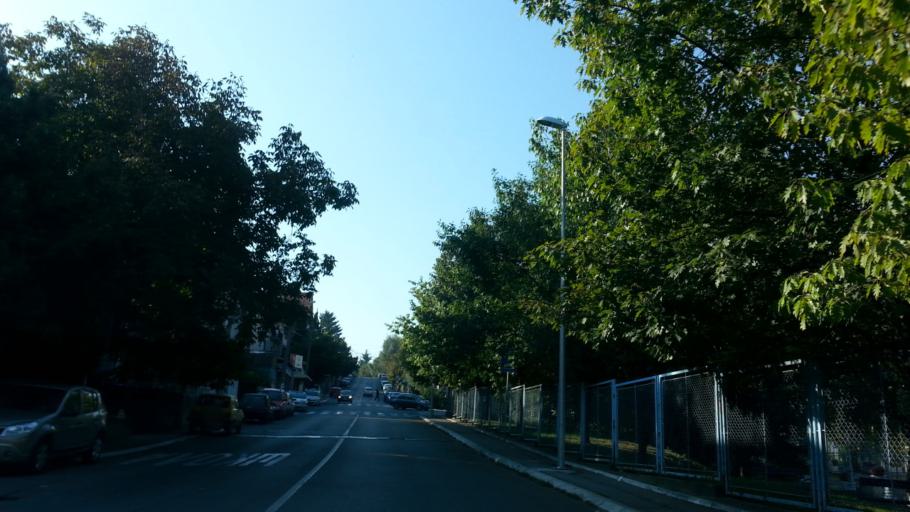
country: RS
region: Central Serbia
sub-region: Belgrade
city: Cukarica
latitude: 44.7647
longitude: 20.4192
